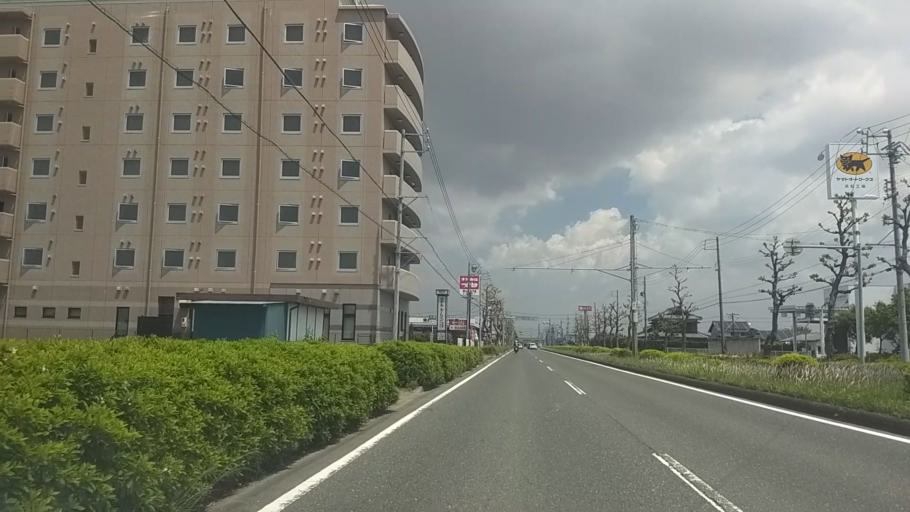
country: JP
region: Shizuoka
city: Hamamatsu
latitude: 34.7662
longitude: 137.6865
